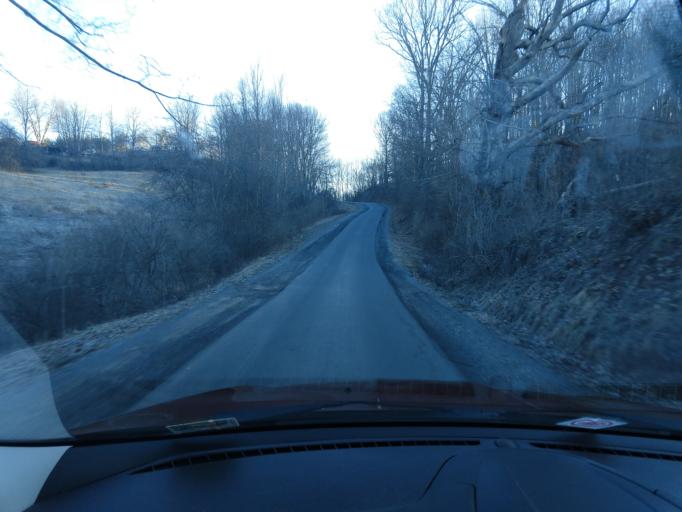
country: US
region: West Virginia
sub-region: Greenbrier County
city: Rainelle
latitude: 37.8707
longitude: -80.7273
